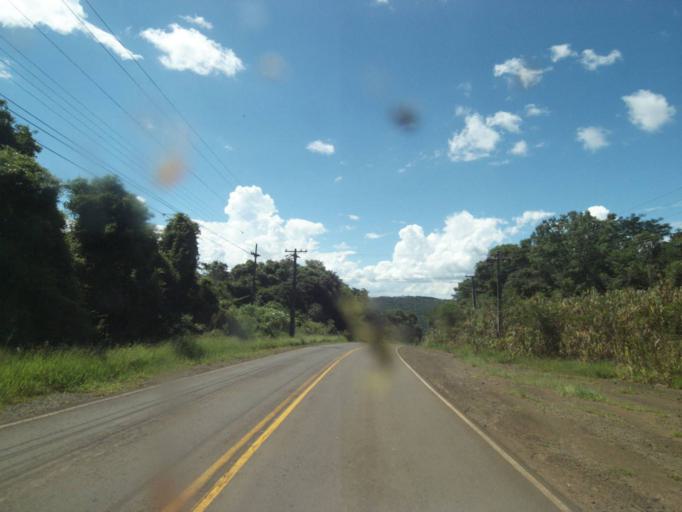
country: BR
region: Parana
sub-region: Chopinzinho
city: Chopinzinho
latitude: -25.7835
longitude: -52.1013
